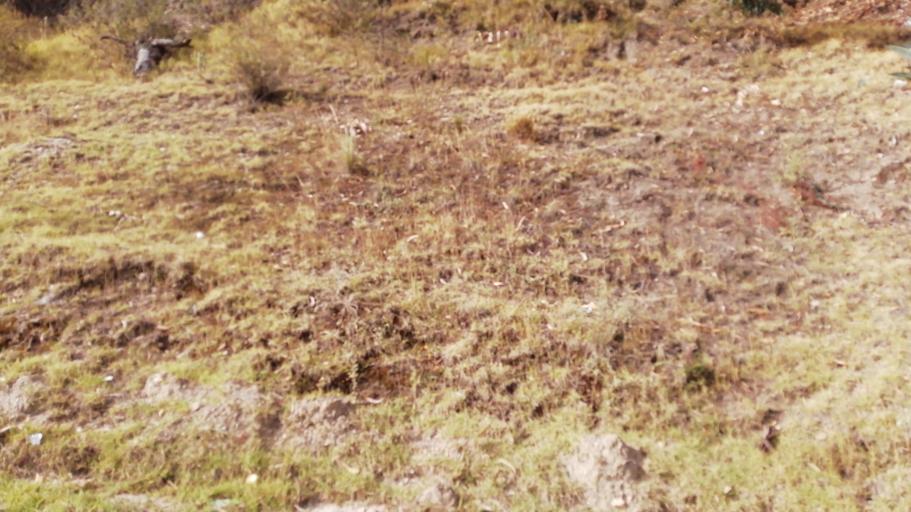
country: CO
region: Boyaca
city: Gameza
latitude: 5.7986
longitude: -72.8035
